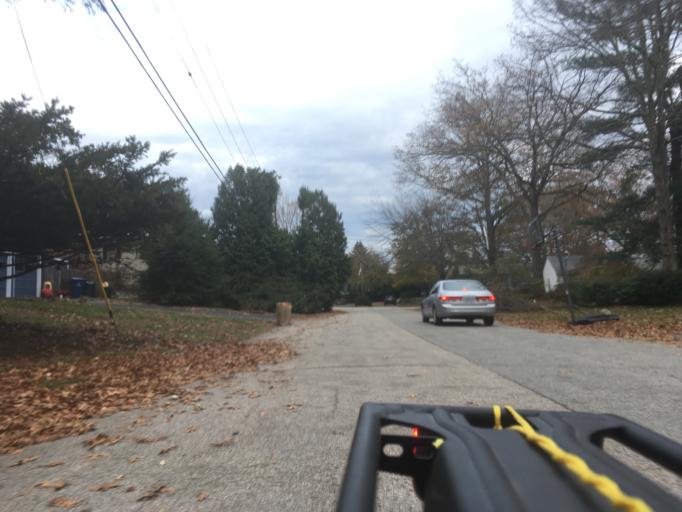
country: US
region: Rhode Island
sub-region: Kent County
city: East Greenwich
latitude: 41.6489
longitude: -71.4676
